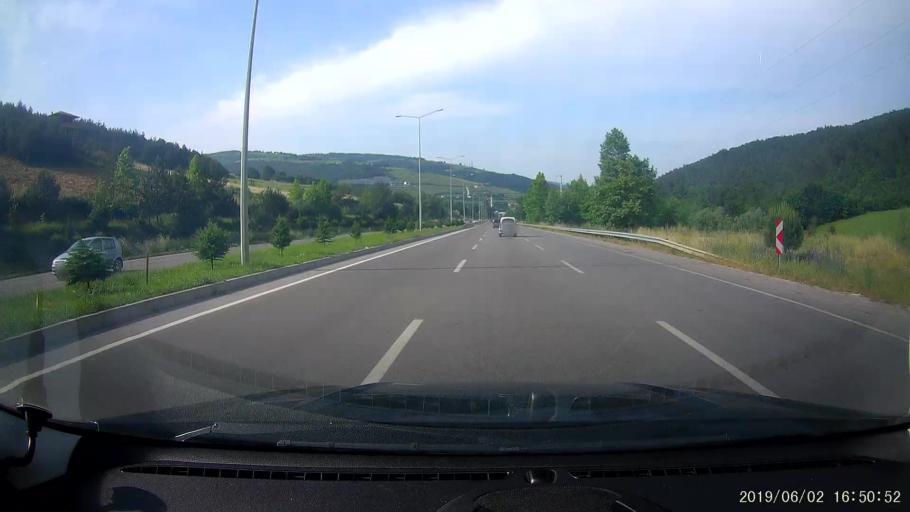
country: TR
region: Samsun
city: Taflan
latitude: 41.2638
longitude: 36.1762
